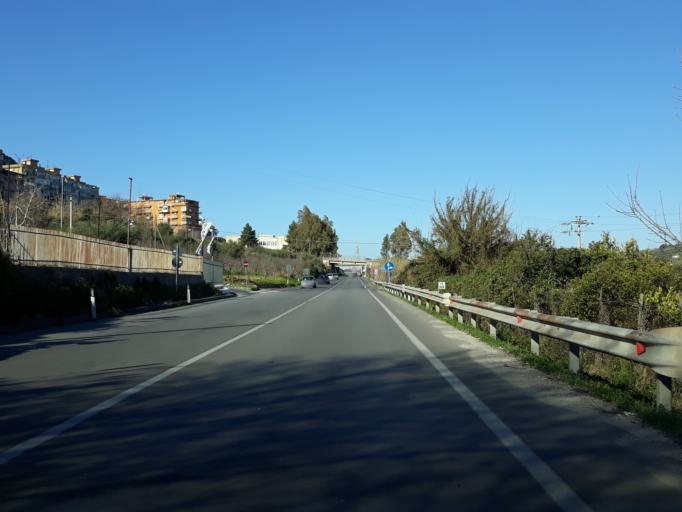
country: IT
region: Sicily
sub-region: Palermo
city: Misilmeri
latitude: 38.0340
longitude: 13.4584
